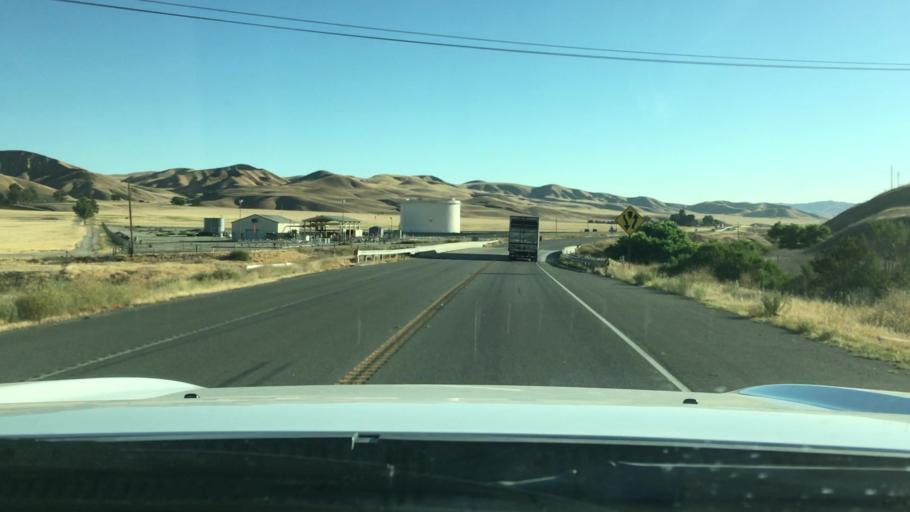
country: US
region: California
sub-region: San Luis Obispo County
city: Shandon
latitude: 35.6872
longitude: -120.3362
